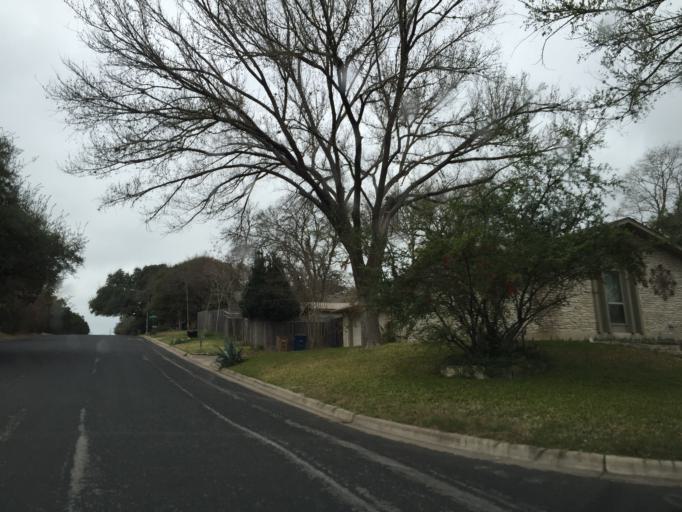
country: US
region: Texas
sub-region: Travis County
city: Wells Branch
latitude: 30.4044
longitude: -97.6821
